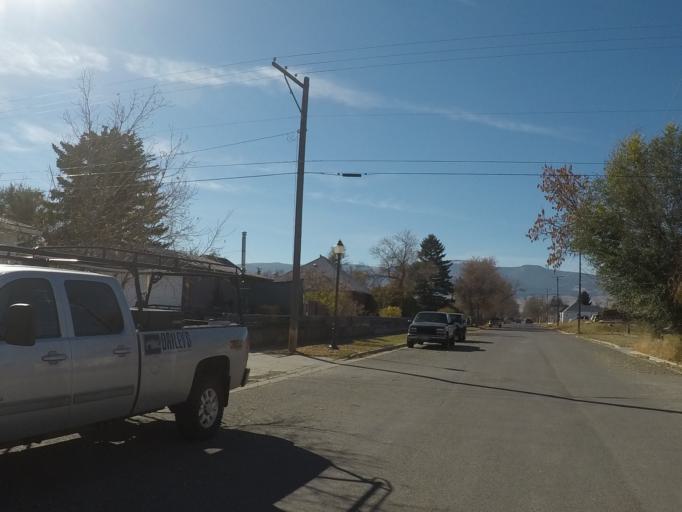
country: US
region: Montana
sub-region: Park County
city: Livingston
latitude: 45.6673
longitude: -110.5491
